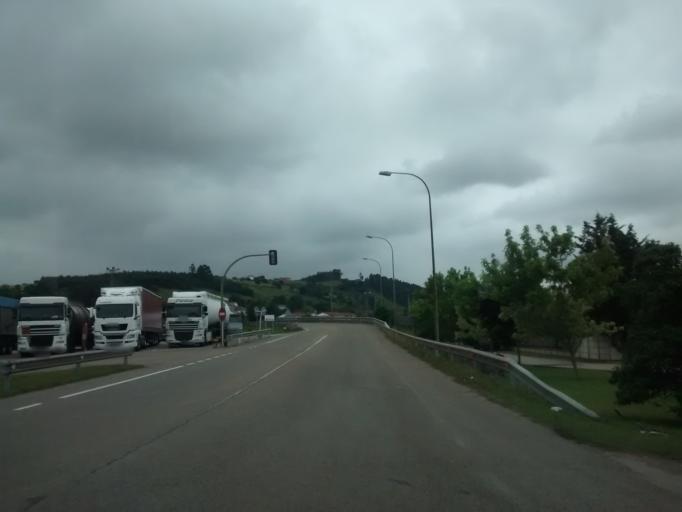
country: ES
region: Cantabria
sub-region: Provincia de Cantabria
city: Torrelavega
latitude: 43.3749
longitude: -4.0434
